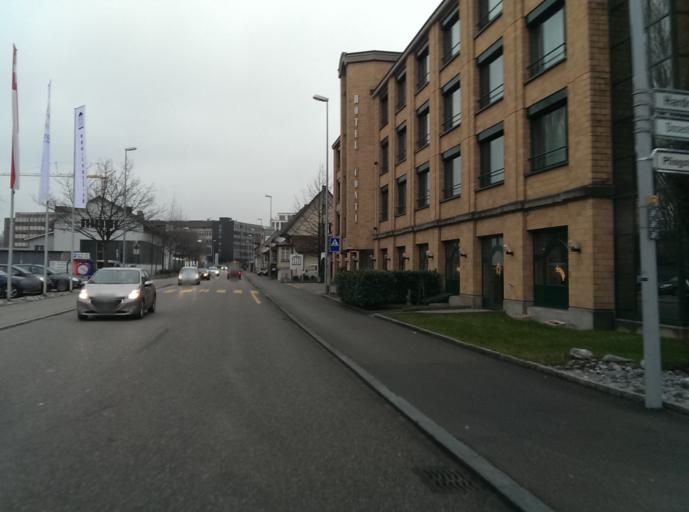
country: CH
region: Zurich
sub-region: Bezirk Dietikon
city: Dietikon / Vorstadt
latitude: 47.4129
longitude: 8.4018
